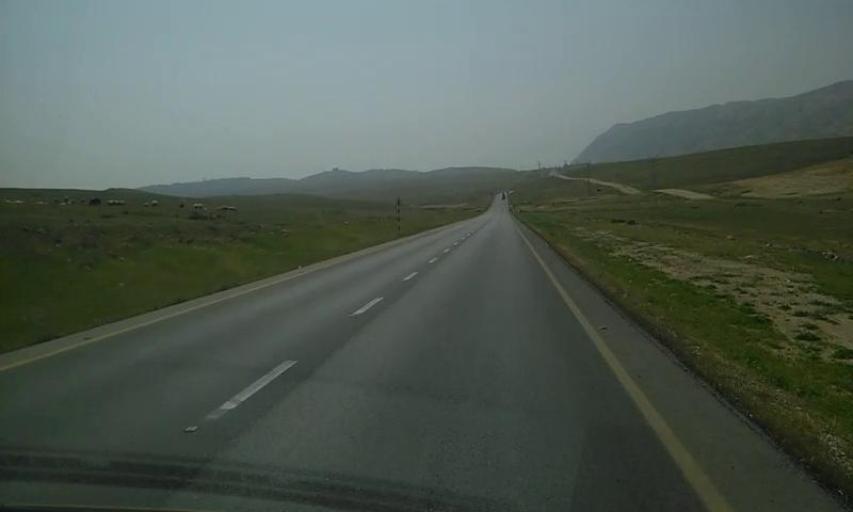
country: PS
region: West Bank
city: An Nuway`imah
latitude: 31.9183
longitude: 35.4193
